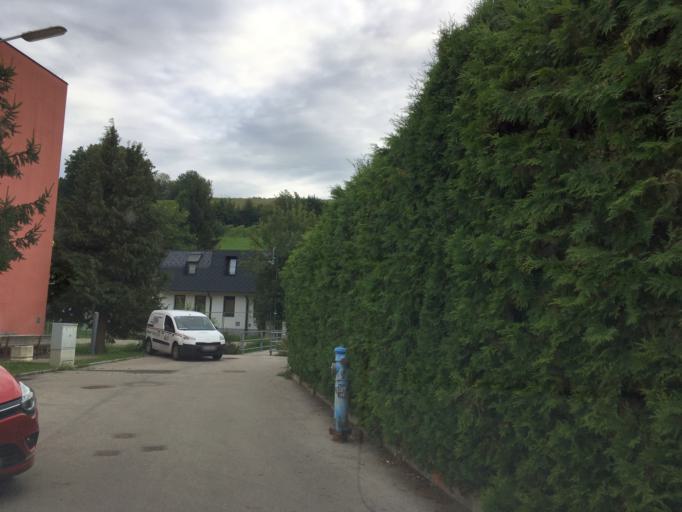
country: AT
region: Lower Austria
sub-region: Politischer Bezirk Tulln
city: Wordern
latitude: 48.3121
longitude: 16.2501
